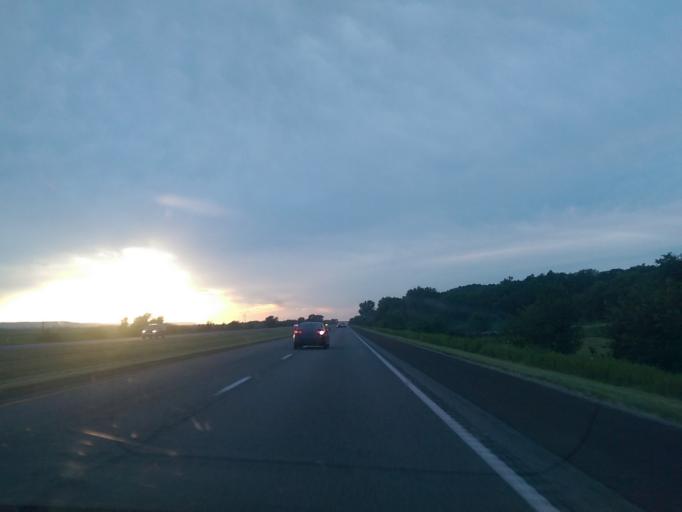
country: US
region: Missouri
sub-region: Holt County
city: Mound City
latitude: 40.2208
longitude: -95.3930
